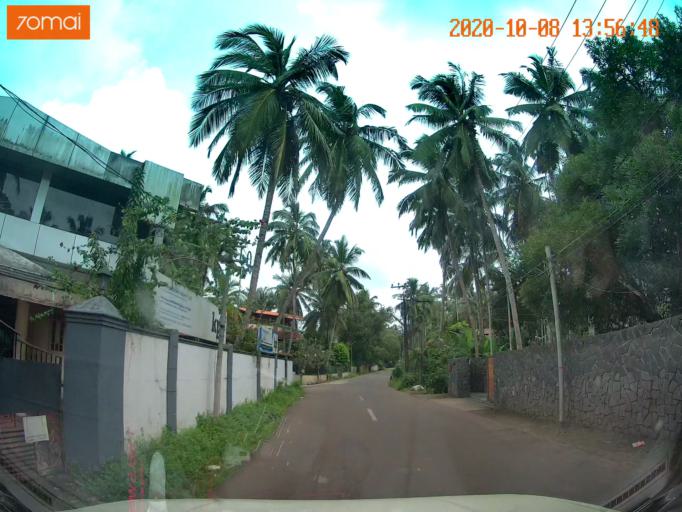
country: IN
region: Kerala
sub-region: Kozhikode
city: Kozhikode
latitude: 11.2917
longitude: 75.8003
